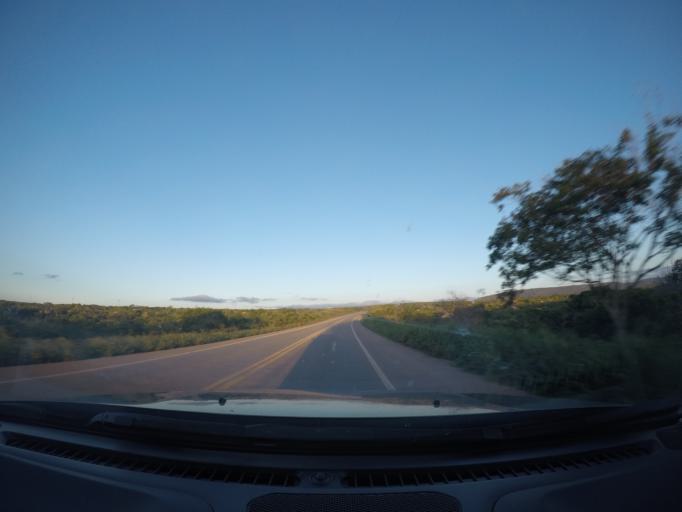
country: BR
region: Bahia
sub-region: Seabra
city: Seabra
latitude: -12.3940
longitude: -41.9271
